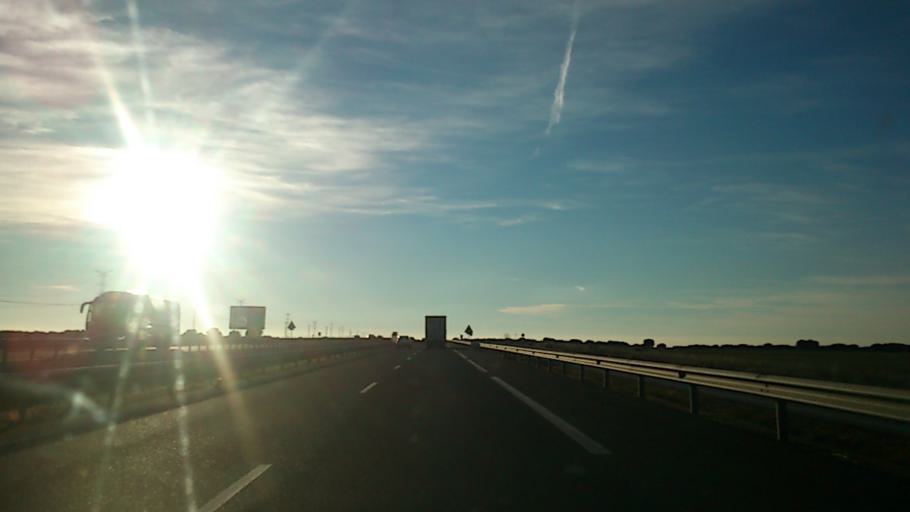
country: ES
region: Castille-La Mancha
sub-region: Provincia de Guadalajara
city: Ledanca
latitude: 40.8516
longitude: -2.8568
